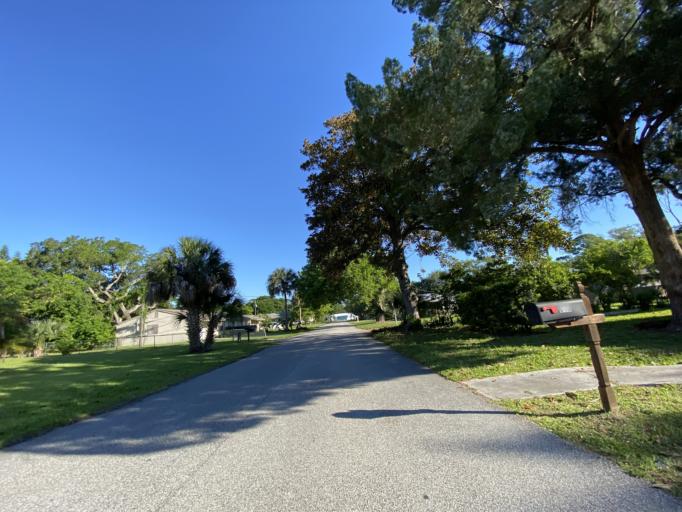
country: US
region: Florida
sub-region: Volusia County
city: Port Orange
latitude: 29.1450
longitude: -80.9905
